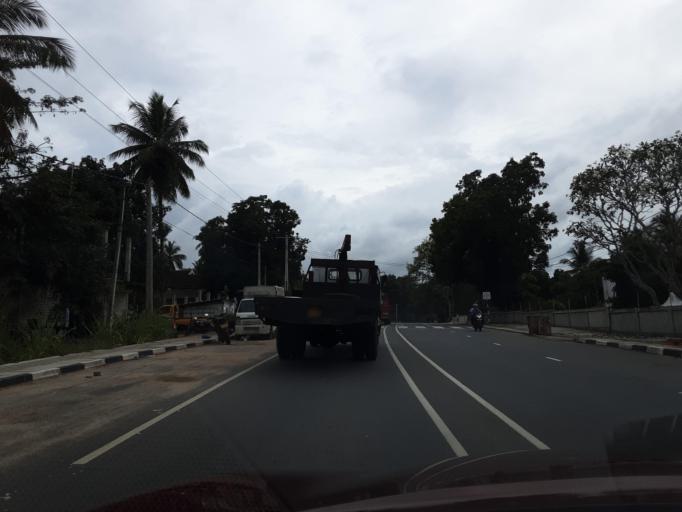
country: LK
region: Uva
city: Badulla
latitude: 7.3967
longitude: 81.2408
